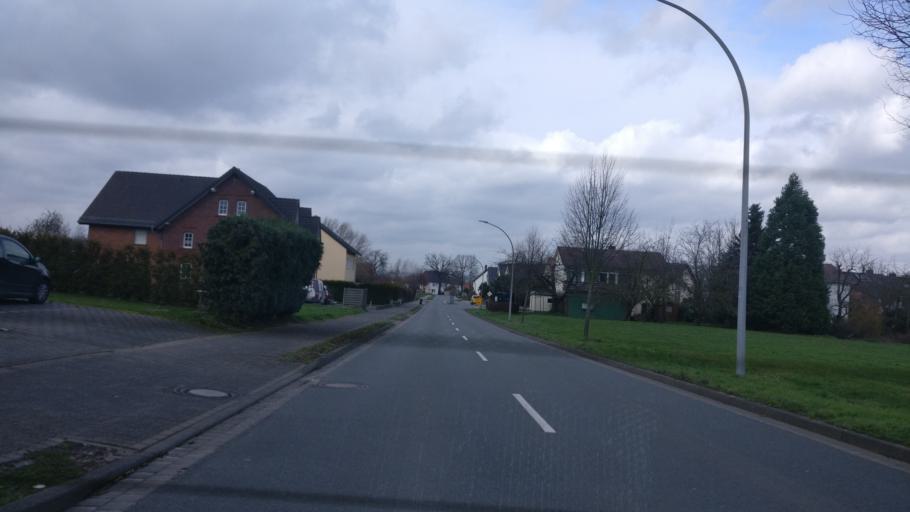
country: DE
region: North Rhine-Westphalia
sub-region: Regierungsbezirk Detmold
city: Lage
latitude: 52.0123
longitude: 8.7932
